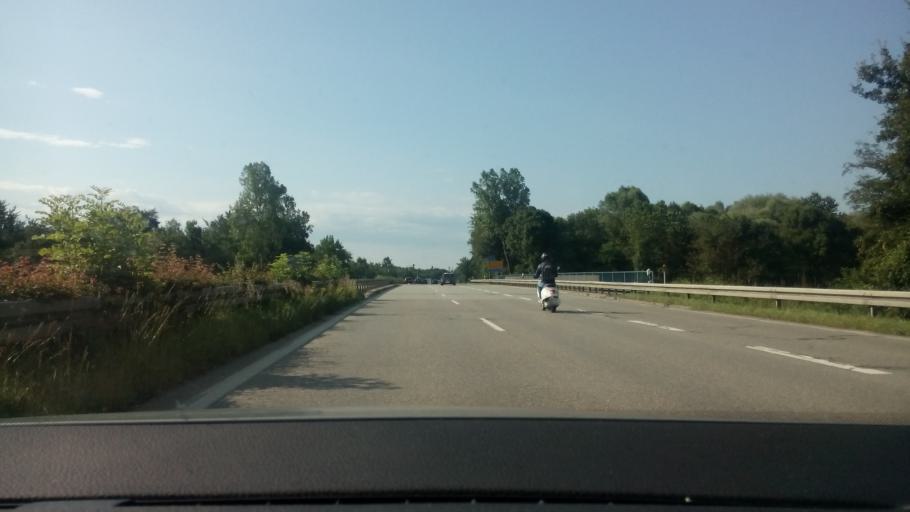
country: DE
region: Bavaria
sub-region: Upper Bavaria
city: Oberschleissheim
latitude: 48.2292
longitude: 11.5861
